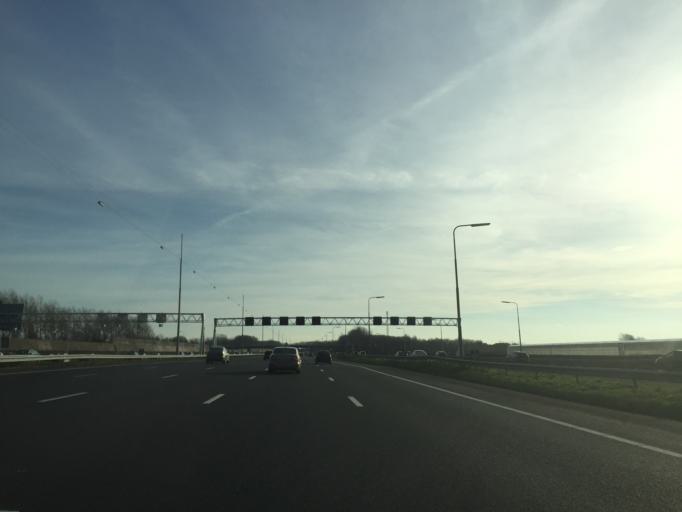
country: NL
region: South Holland
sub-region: Gemeente Ridderkerk
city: Ridderkerk
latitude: 51.8670
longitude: 4.5824
